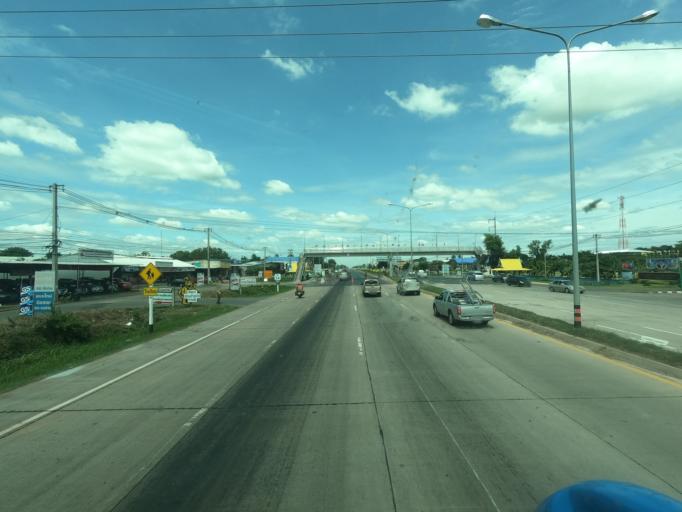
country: TH
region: Surin
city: Prasat
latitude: 14.6304
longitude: 103.4078
